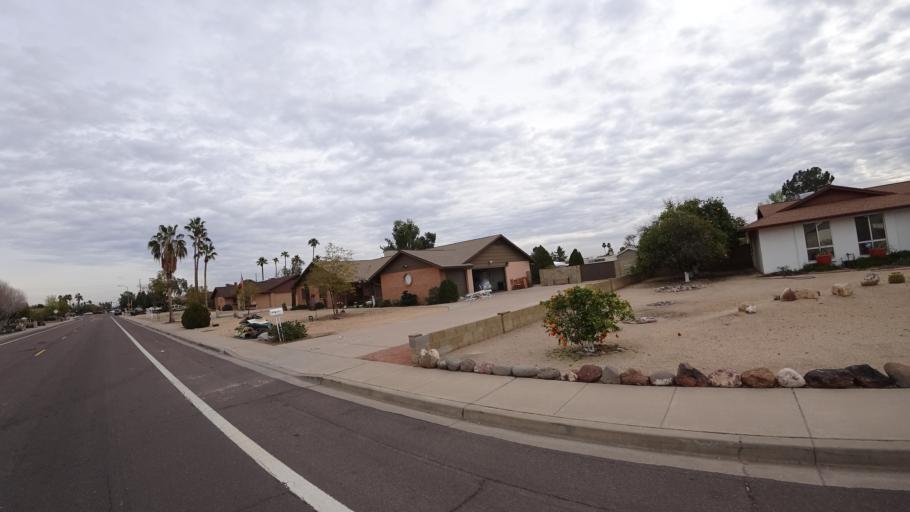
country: US
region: Arizona
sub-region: Maricopa County
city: Peoria
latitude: 33.6471
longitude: -112.1891
